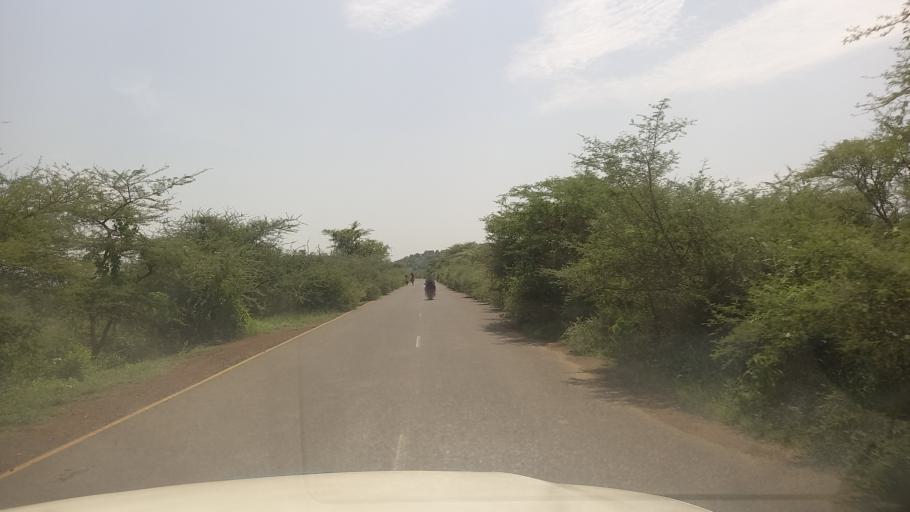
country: ET
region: Gambela
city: Gambela
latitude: 8.2816
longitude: 34.2222
